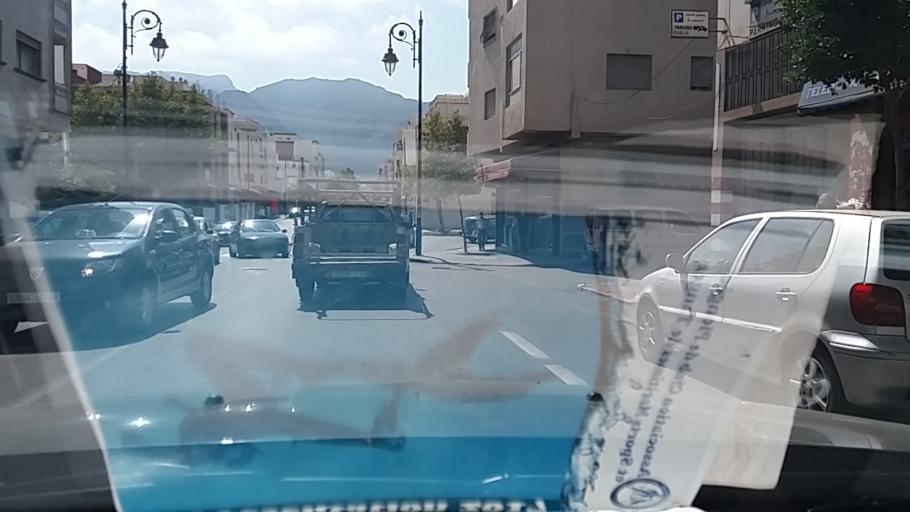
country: MA
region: Tanger-Tetouan
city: Tetouan
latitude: 35.5660
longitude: -5.3578
